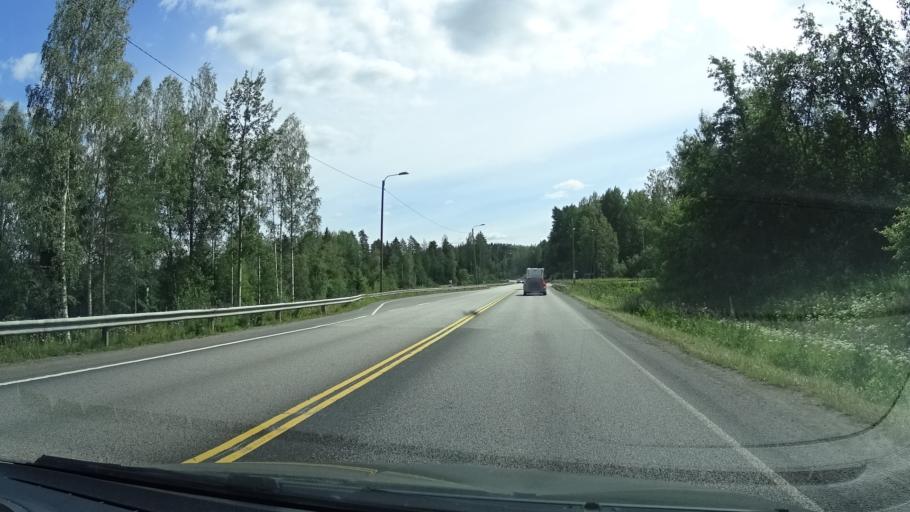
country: FI
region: Central Finland
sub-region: Jyvaeskylae
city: Jyvaeskylae
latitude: 62.2675
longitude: 25.5556
